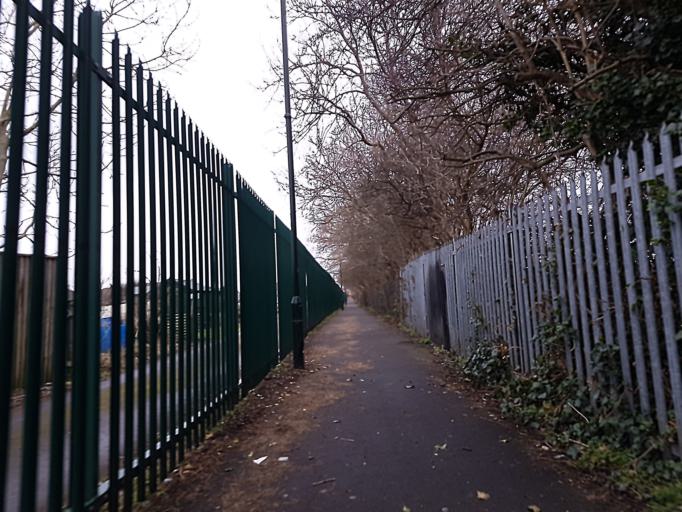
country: GB
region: England
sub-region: North East Lincolnshire
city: Grimbsy
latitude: 53.5599
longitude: -0.1030
